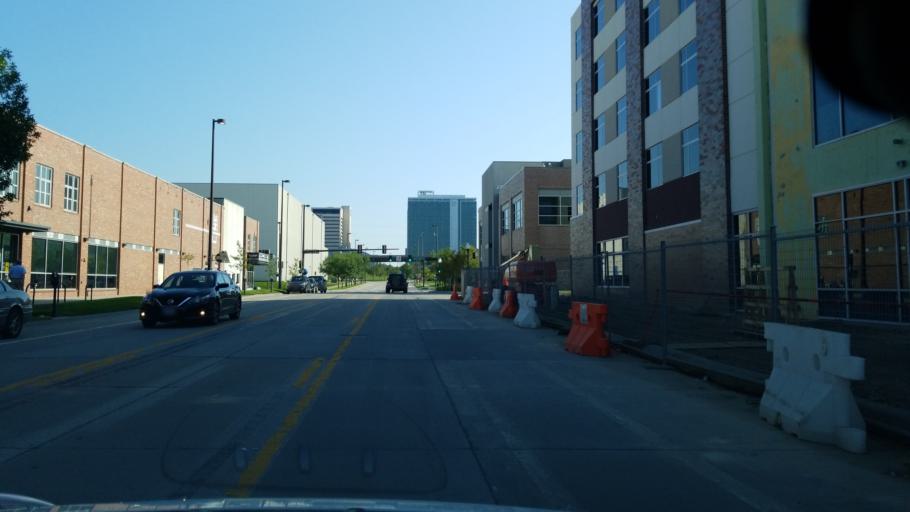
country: US
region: Nebraska
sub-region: Douglas County
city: Omaha
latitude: 41.2669
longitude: -95.9345
